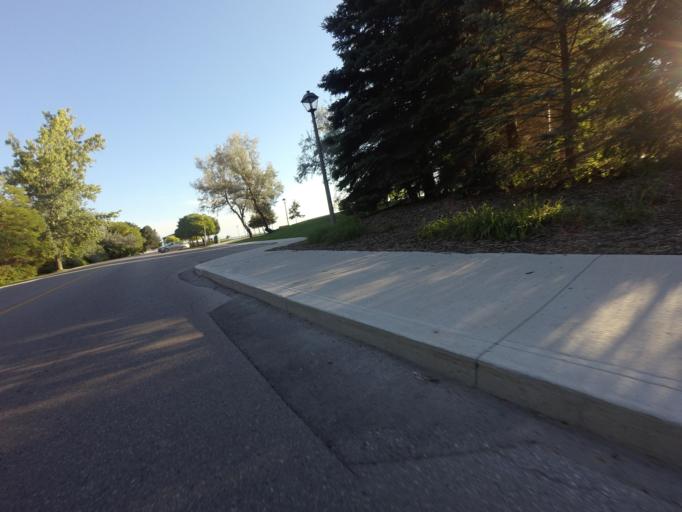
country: CA
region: Ontario
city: Goderich
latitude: 43.7387
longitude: -81.7260
